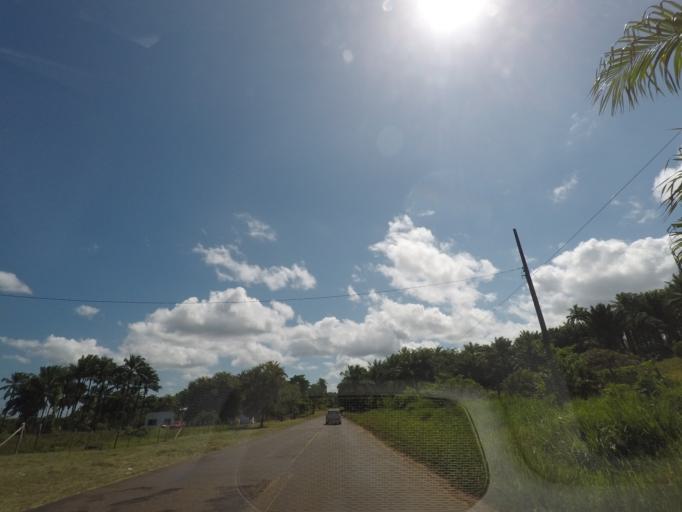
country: BR
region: Bahia
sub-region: Taperoa
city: Taperoa
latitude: -13.5514
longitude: -39.1009
